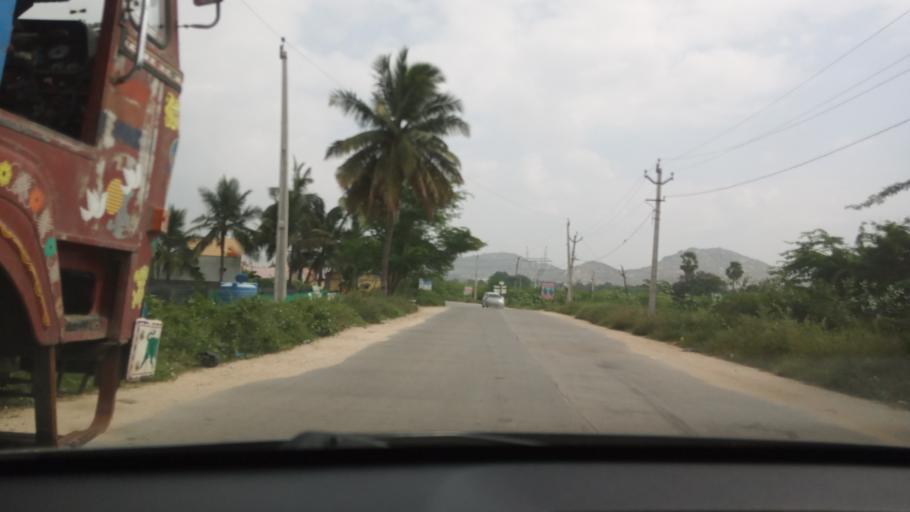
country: IN
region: Andhra Pradesh
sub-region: Chittoor
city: Madanapalle
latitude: 13.6523
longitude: 78.8085
